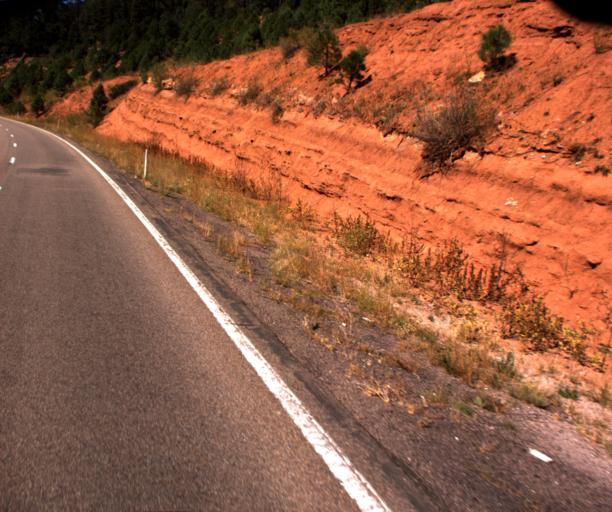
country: US
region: Arizona
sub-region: Gila County
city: Star Valley
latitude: 34.3071
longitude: -110.9323
